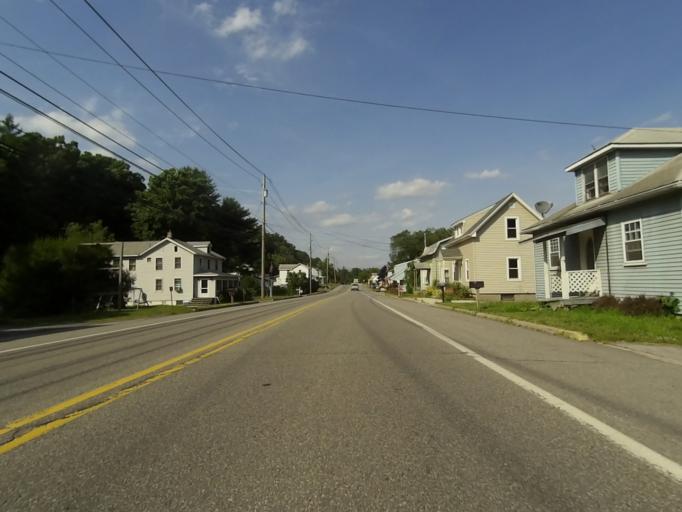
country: US
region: Pennsylvania
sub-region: Centre County
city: Stormstown
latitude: 40.8020
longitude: -78.0513
